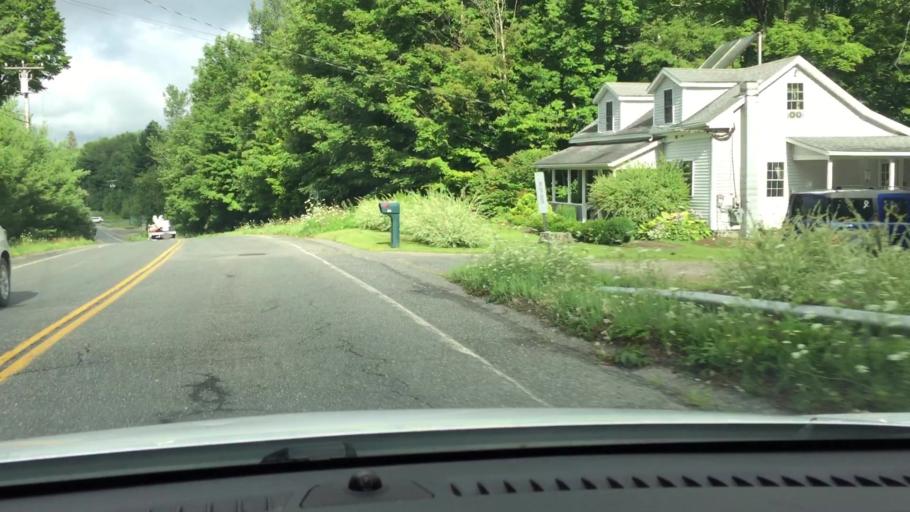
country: US
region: Massachusetts
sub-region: Berkshire County
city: Hinsdale
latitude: 42.4460
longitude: -73.0772
